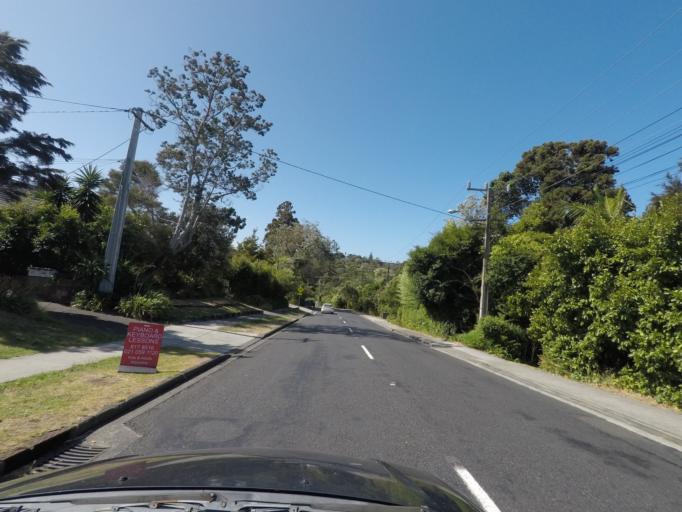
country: NZ
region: Auckland
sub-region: Auckland
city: Waitakere
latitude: -36.9257
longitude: 174.6552
